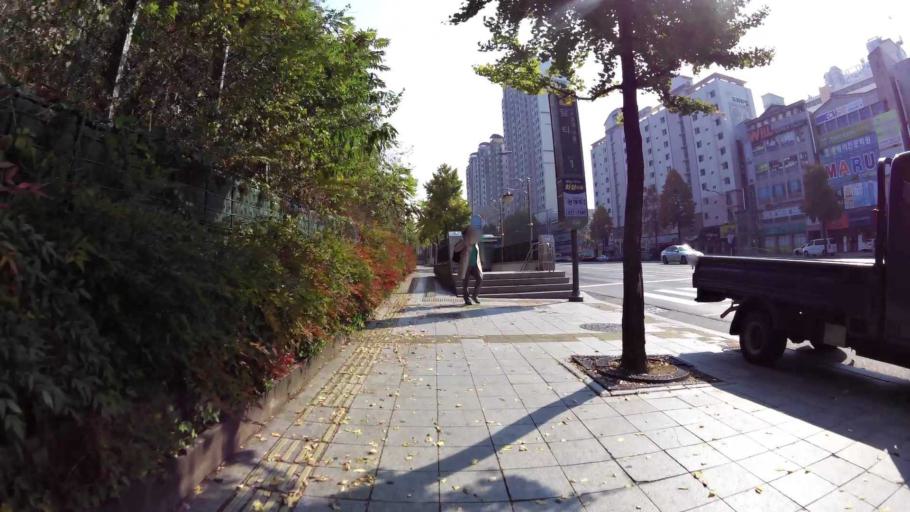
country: KR
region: Daegu
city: Daegu
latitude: 35.8555
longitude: 128.6534
